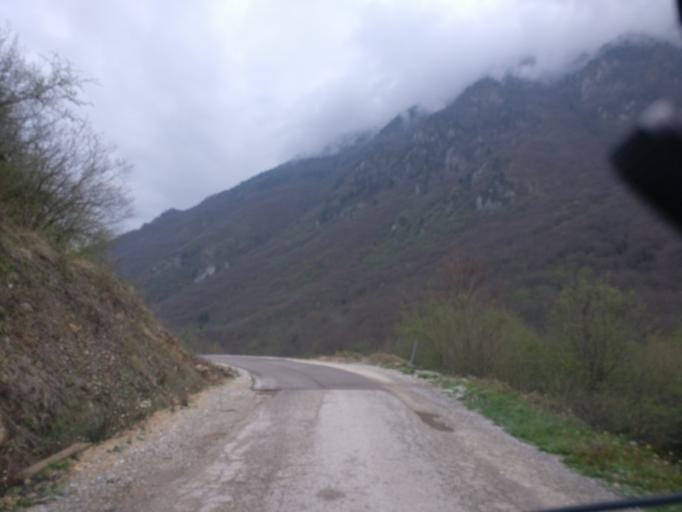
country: BA
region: Republika Srpska
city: Foca
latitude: 43.3598
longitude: 18.8122
